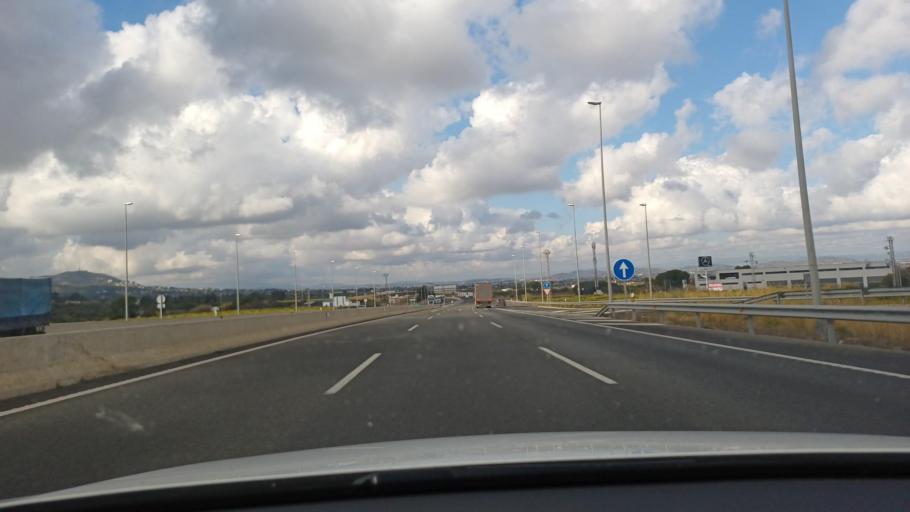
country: ES
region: Valencia
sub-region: Provincia de Valencia
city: Torrent
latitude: 39.4176
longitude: -0.5100
